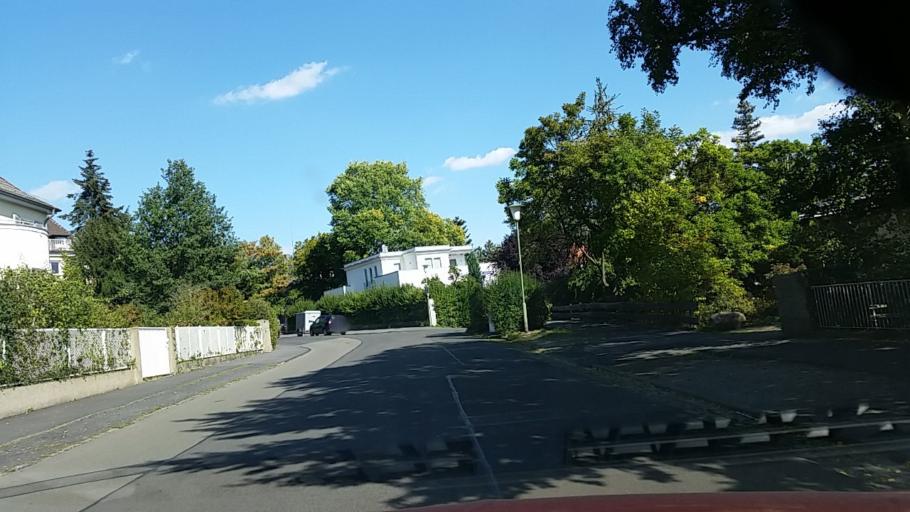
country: DE
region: Hesse
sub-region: Regierungsbezirk Kassel
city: Baunatal
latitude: 51.3083
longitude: 9.4165
